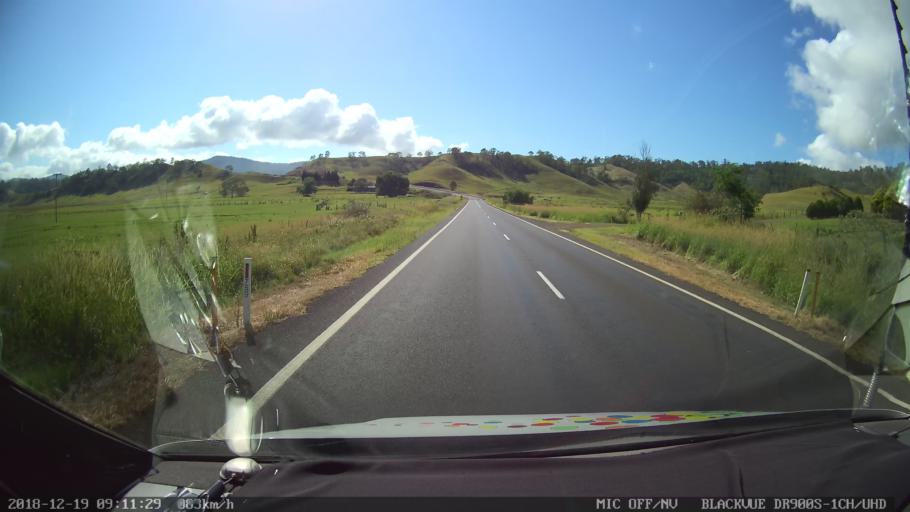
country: AU
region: New South Wales
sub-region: Kyogle
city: Kyogle
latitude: -28.4934
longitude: 152.9388
